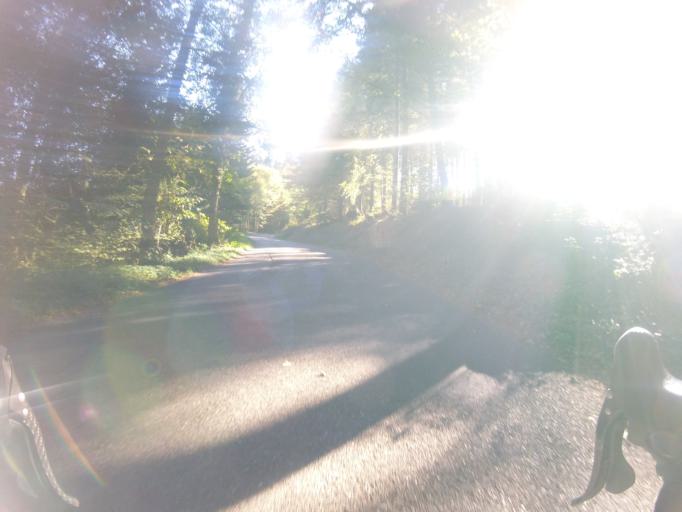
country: CH
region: Bern
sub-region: Seeland District
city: Schupfen
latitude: 47.0339
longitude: 7.3917
